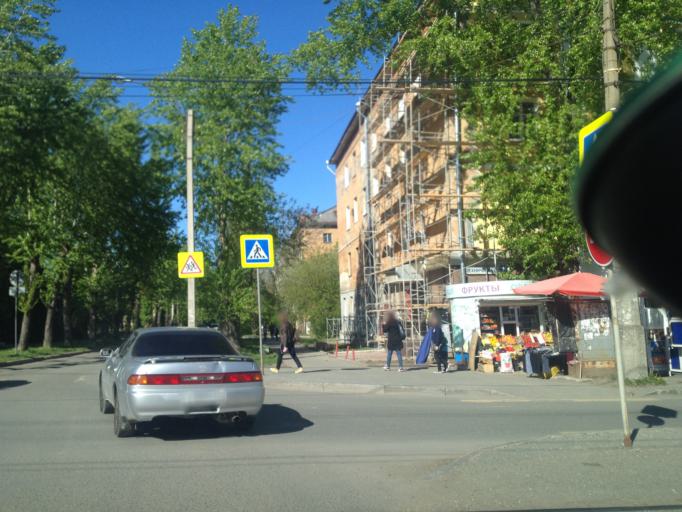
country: RU
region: Sverdlovsk
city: Shuvakish
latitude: 56.8685
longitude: 60.5264
